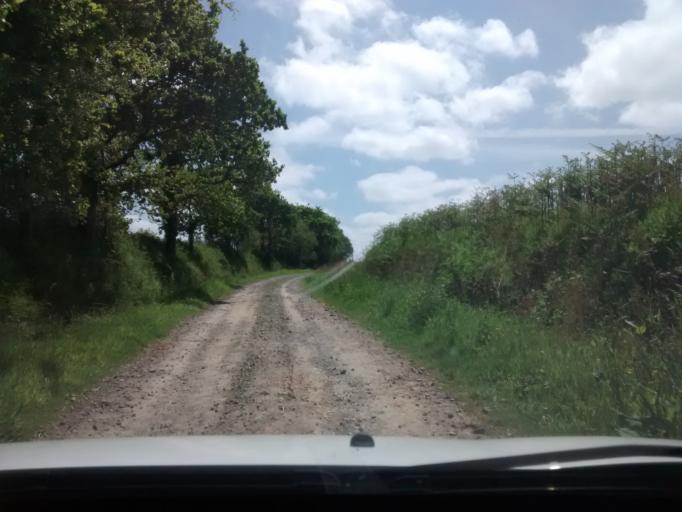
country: FR
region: Brittany
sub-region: Departement des Cotes-d'Armor
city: Louannec
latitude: 48.7833
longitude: -3.4084
